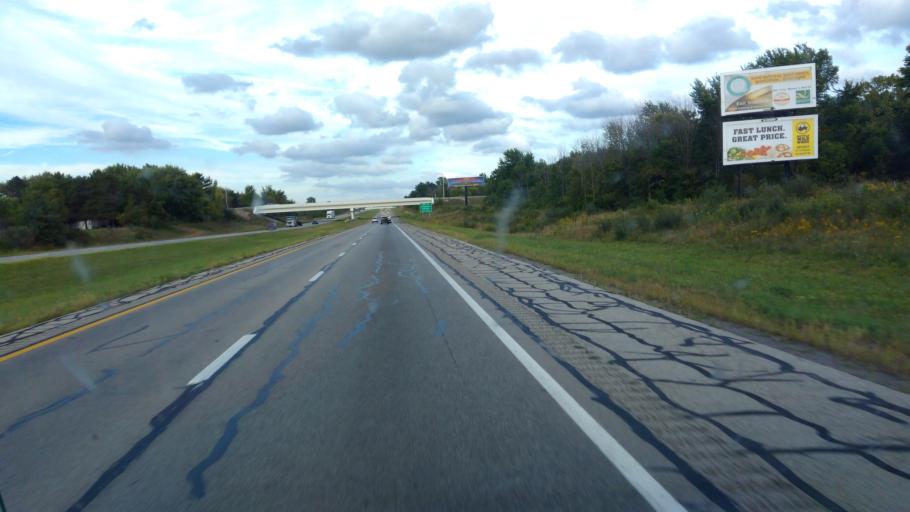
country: US
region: Ohio
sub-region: Crawford County
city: Crestline
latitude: 40.7664
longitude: -82.6832
